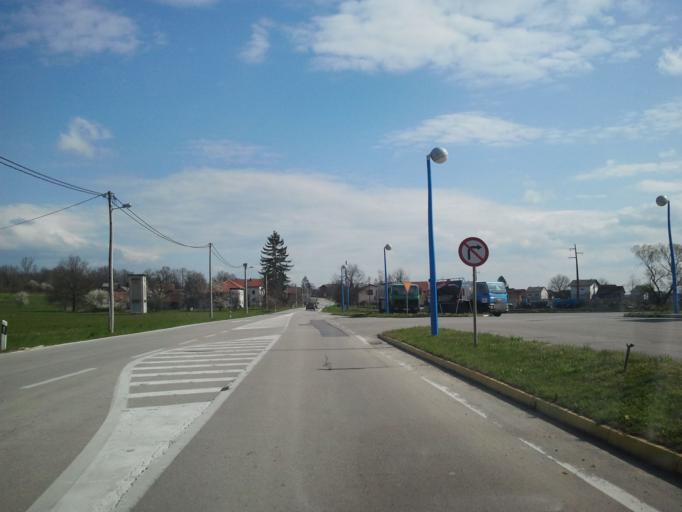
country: HR
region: Karlovacka
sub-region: Grad Karlovac
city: Karlovac
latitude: 45.5659
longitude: 15.5869
